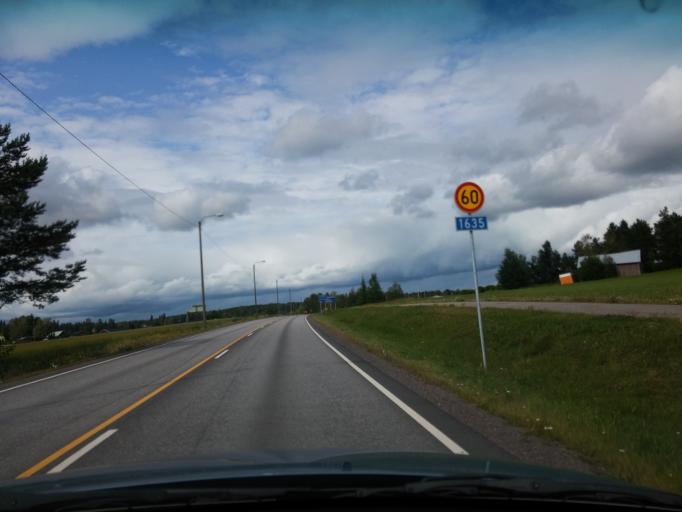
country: FI
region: Uusimaa
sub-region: Porvoo
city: Askola
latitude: 60.5217
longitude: 25.5794
